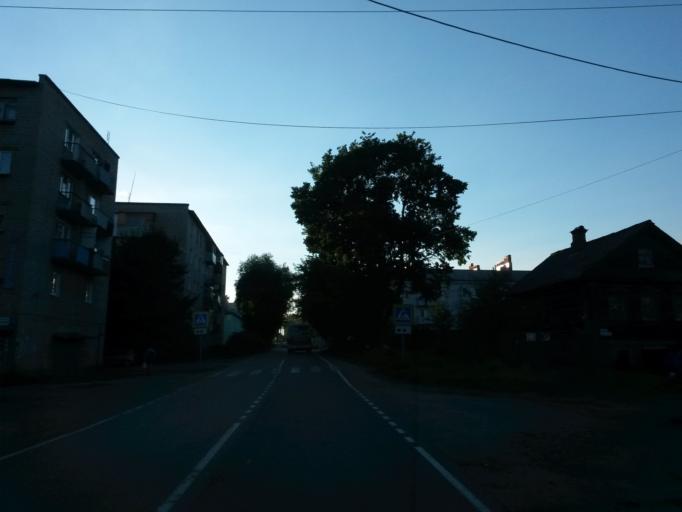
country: RU
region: Jaroslavl
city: Tutayev
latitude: 57.8748
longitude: 39.5206
